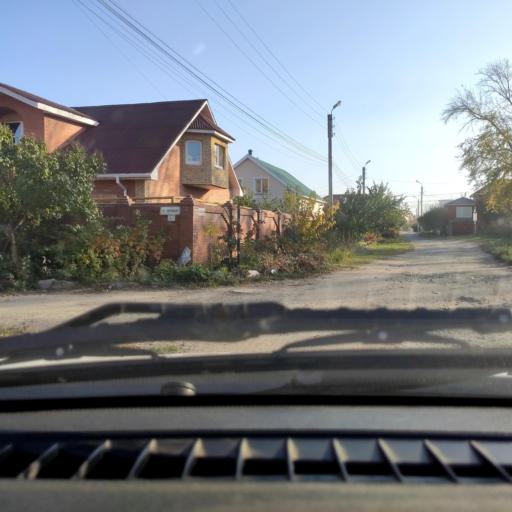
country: RU
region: Samara
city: Tol'yatti
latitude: 53.5354
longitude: 49.4055
